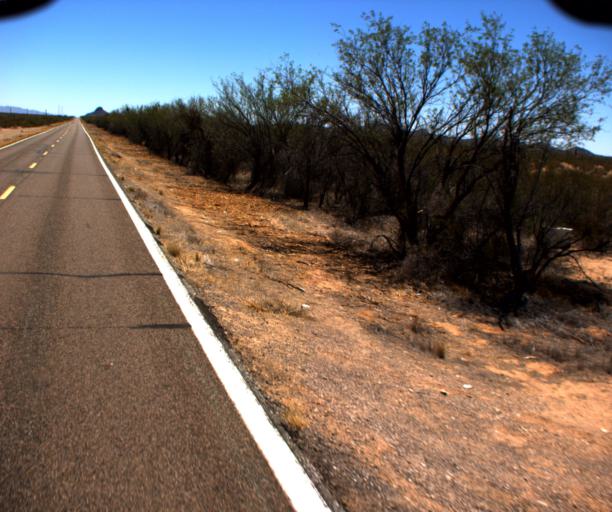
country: US
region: Arizona
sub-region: Pima County
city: Ajo
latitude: 32.2077
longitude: -112.5921
